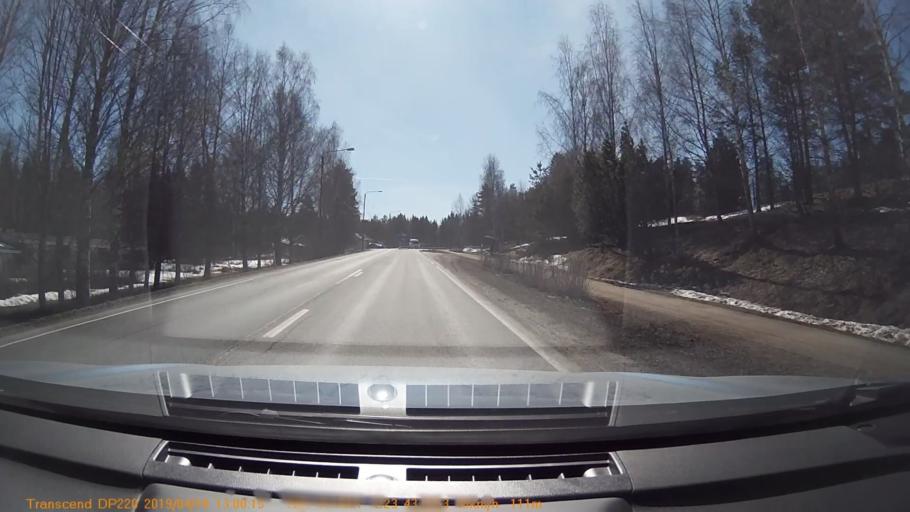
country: FI
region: Pirkanmaa
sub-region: Tampere
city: Kuru
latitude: 61.8713
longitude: 23.7268
